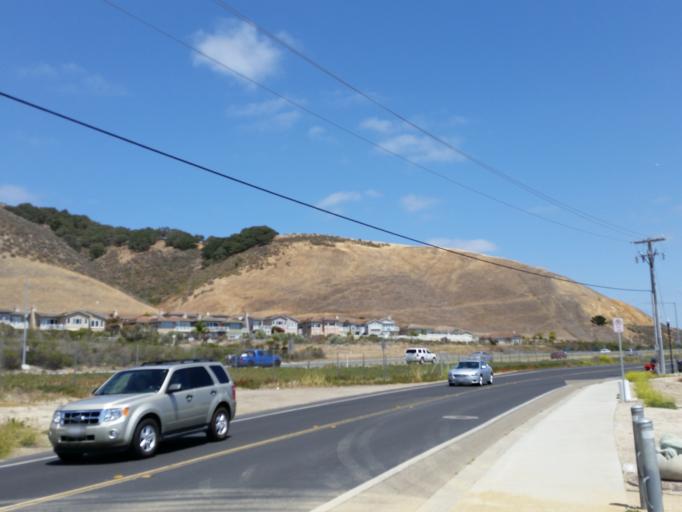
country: US
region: California
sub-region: San Luis Obispo County
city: Pismo Beach
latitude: 35.1540
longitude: -120.6632
